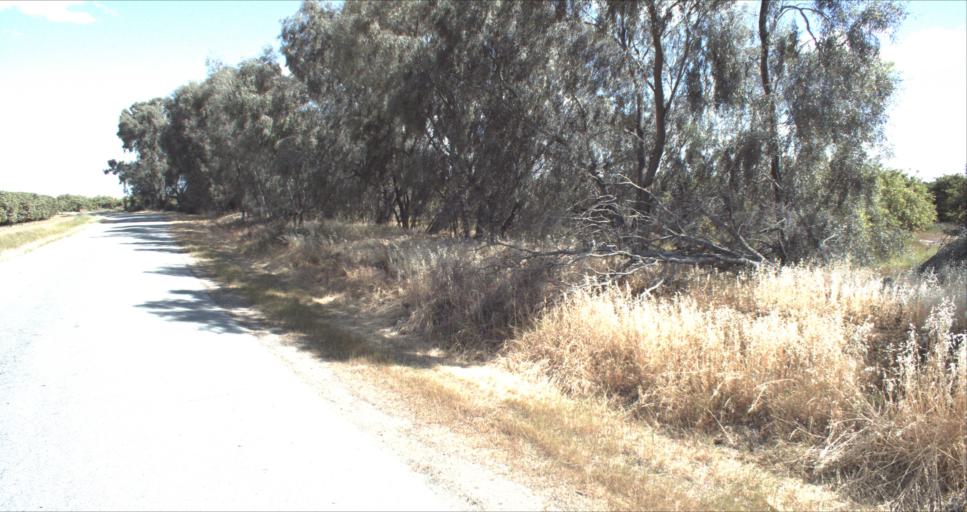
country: AU
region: New South Wales
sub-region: Leeton
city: Leeton
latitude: -34.5085
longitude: 146.2243
